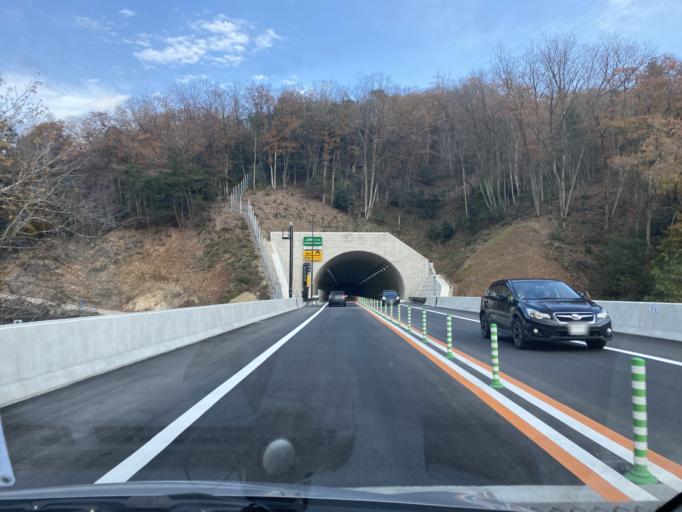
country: JP
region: Hyogo
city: Toyooka
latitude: 35.4988
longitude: 134.7900
